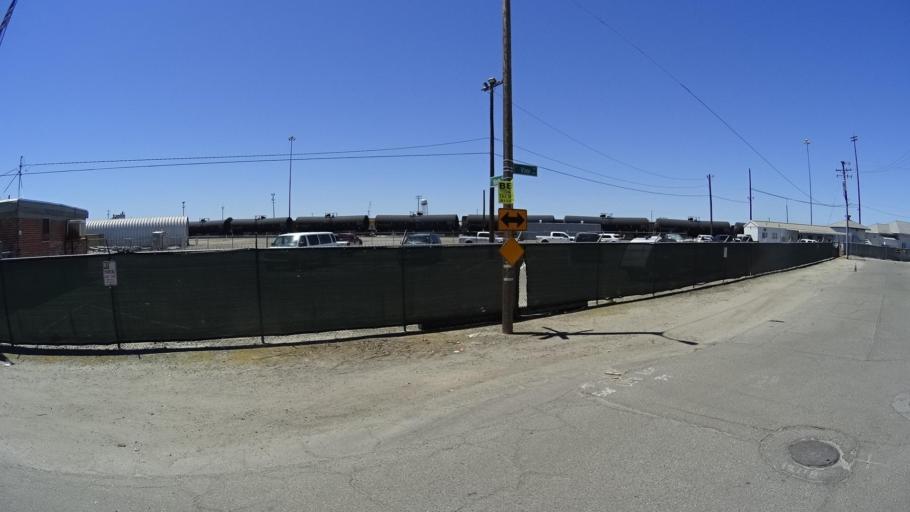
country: US
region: California
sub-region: Fresno County
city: Fresno
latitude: 36.7033
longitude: -119.7585
